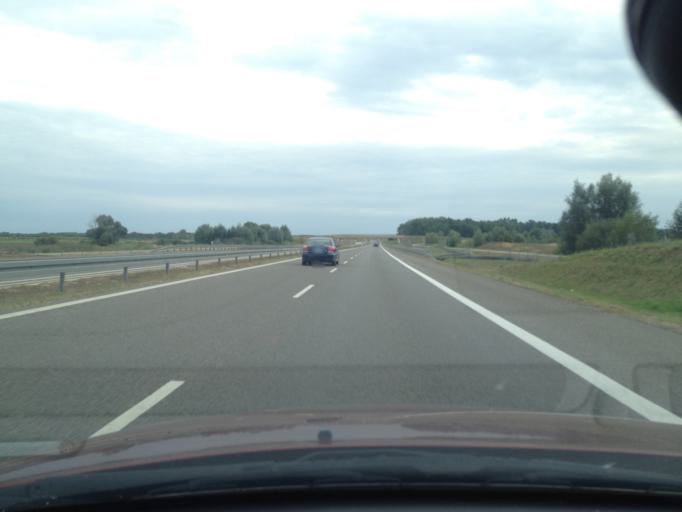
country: PL
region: West Pomeranian Voivodeship
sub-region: Powiat mysliborski
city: Nowogrodek Pomorski
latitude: 52.9019
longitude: 15.0195
